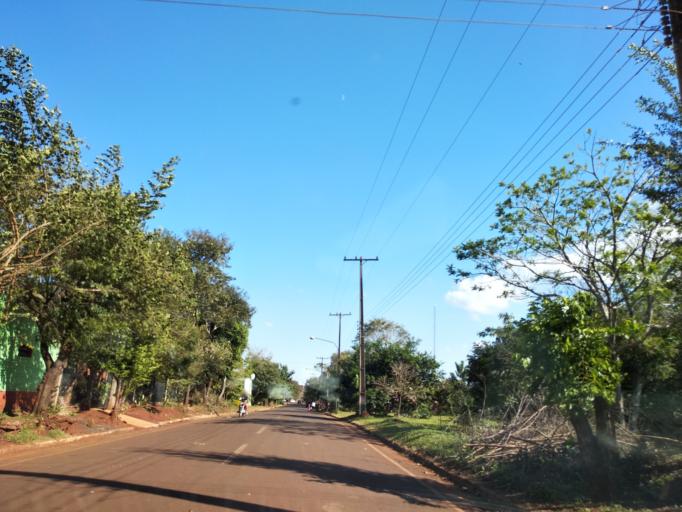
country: PY
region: Itapua
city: Hohenau
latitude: -27.0555
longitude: -55.7429
